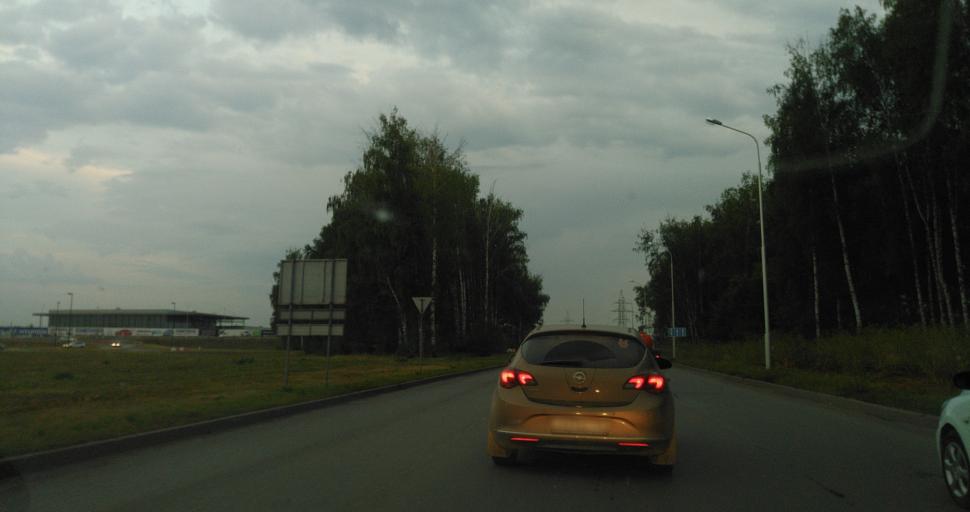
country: RU
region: Bashkortostan
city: Ufa
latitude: 54.6716
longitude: 55.9255
